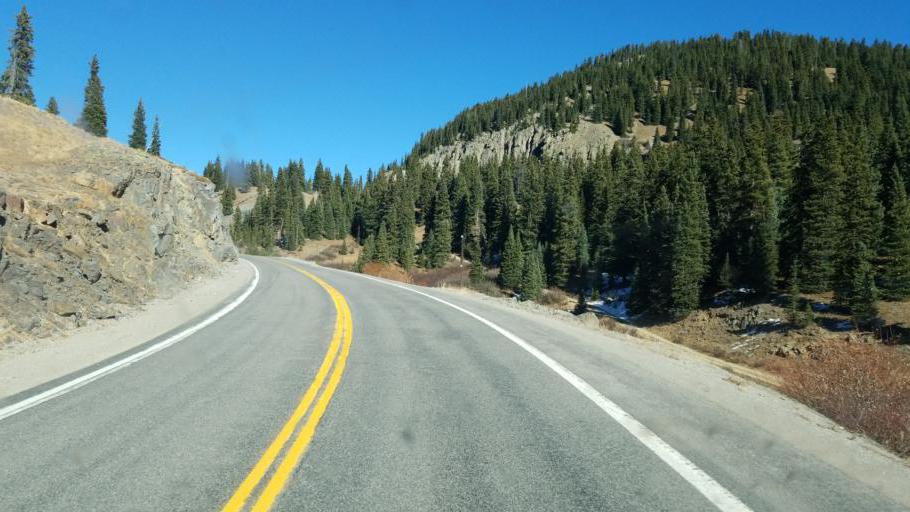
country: US
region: Colorado
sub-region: San Juan County
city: Silverton
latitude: 37.8923
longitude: -107.7162
